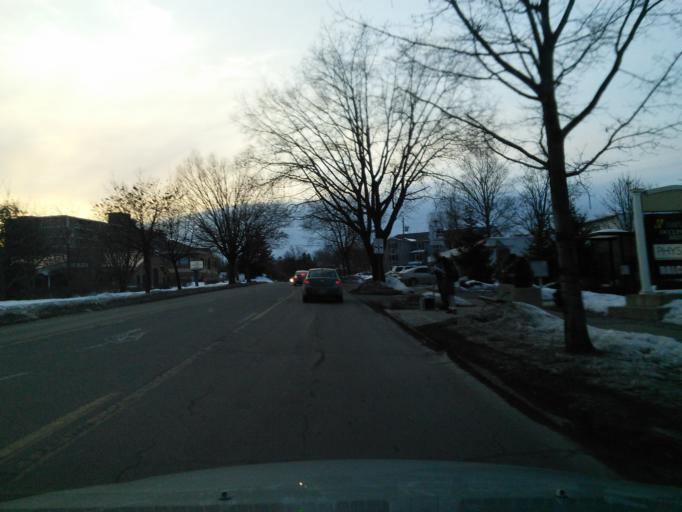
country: US
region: Pennsylvania
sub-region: Centre County
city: State College
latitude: 40.7859
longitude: -77.8551
